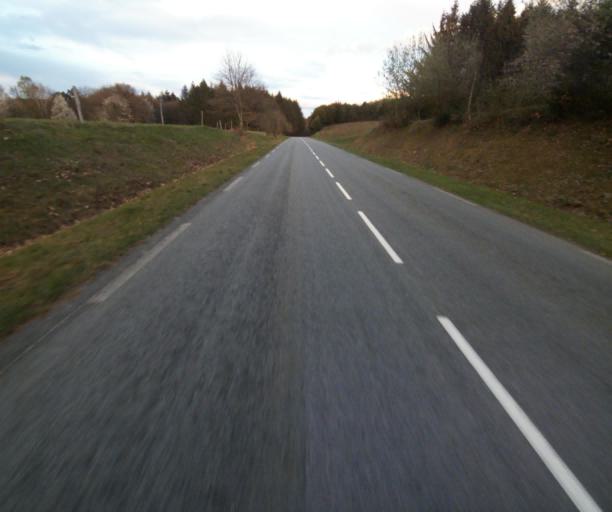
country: FR
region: Limousin
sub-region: Departement de la Correze
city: Laguenne
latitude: 45.2870
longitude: 1.8547
